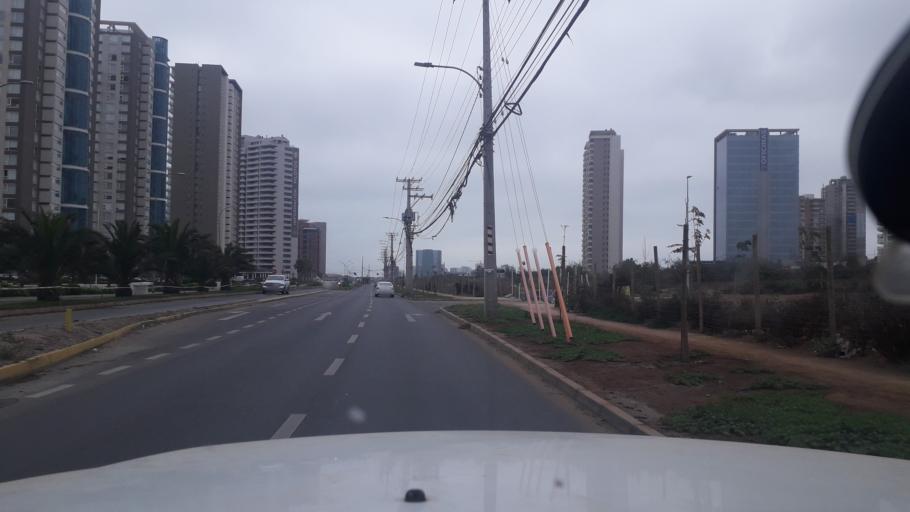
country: CL
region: Valparaiso
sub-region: Provincia de Valparaiso
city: Vina del Mar
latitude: -32.9526
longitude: -71.5440
